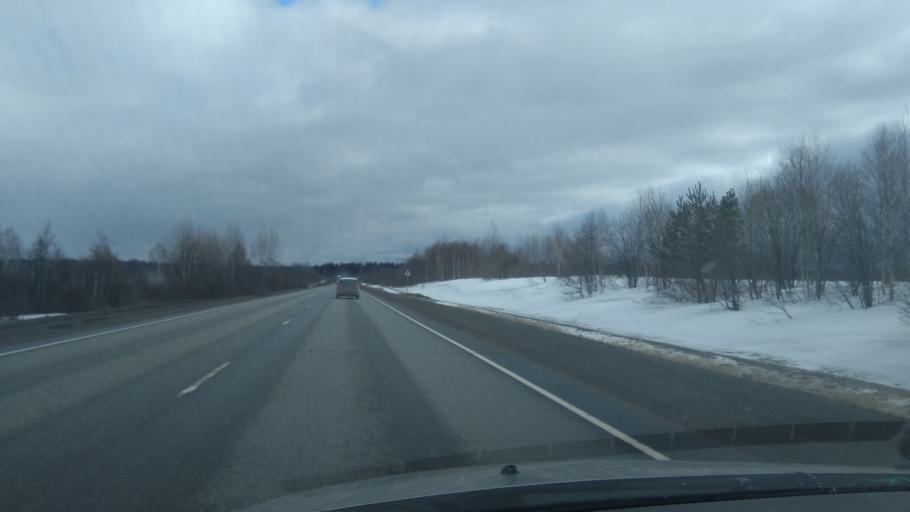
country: RU
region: Sverdlovsk
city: Ufimskiy
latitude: 56.7718
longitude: 58.0784
